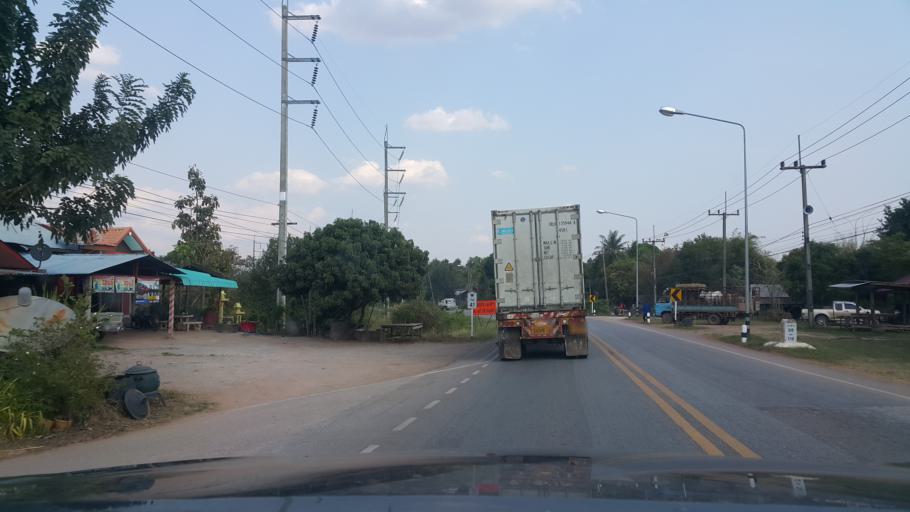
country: TH
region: Phitsanulok
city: Nakhon Thai
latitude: 17.1333
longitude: 100.9269
